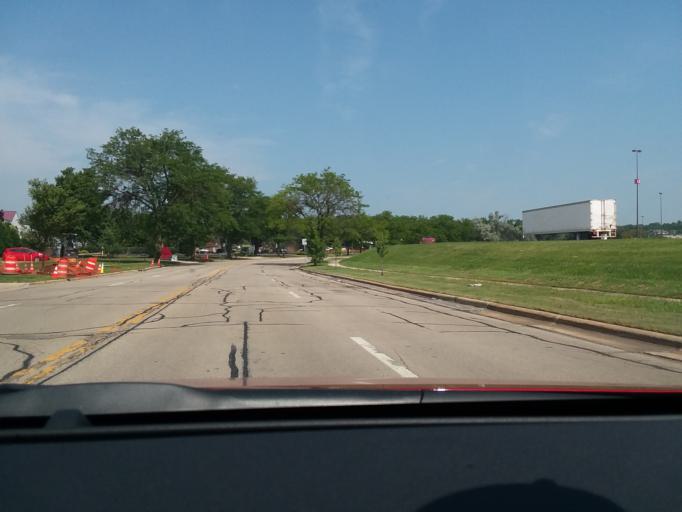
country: US
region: Wisconsin
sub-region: Dane County
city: Monona
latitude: 43.1227
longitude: -89.3079
